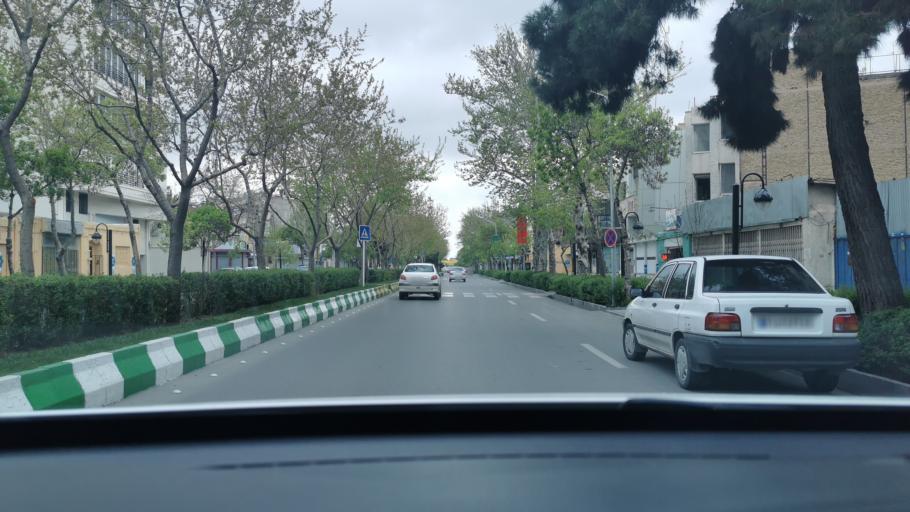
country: IR
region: Razavi Khorasan
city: Mashhad
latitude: 36.2790
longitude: 59.5945
